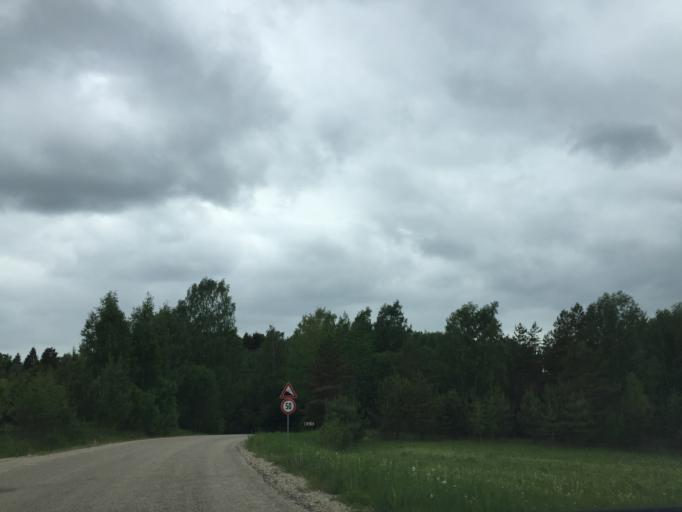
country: LV
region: Aglona
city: Aglona
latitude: 56.0728
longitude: 26.9004
